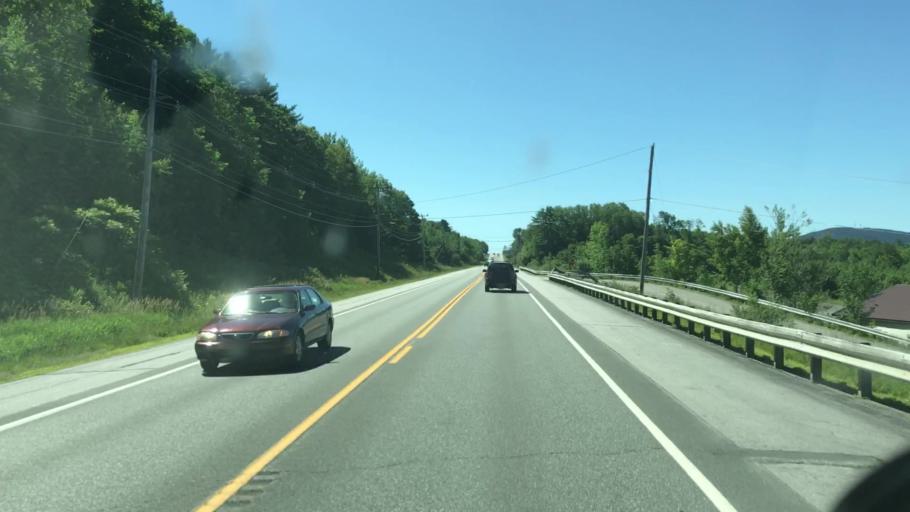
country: US
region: Maine
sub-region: Hancock County
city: Dedham
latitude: 44.7133
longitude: -68.6043
